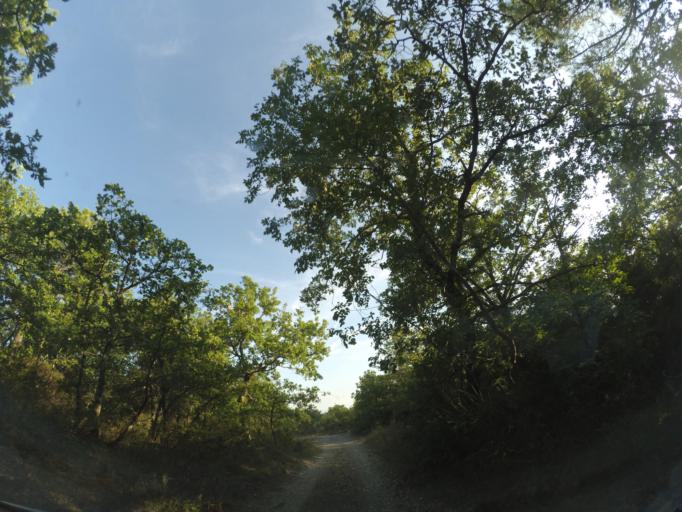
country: IT
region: Tuscany
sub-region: Province of Arezzo
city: Castiglion Fibocchi
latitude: 43.5474
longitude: 11.7882
